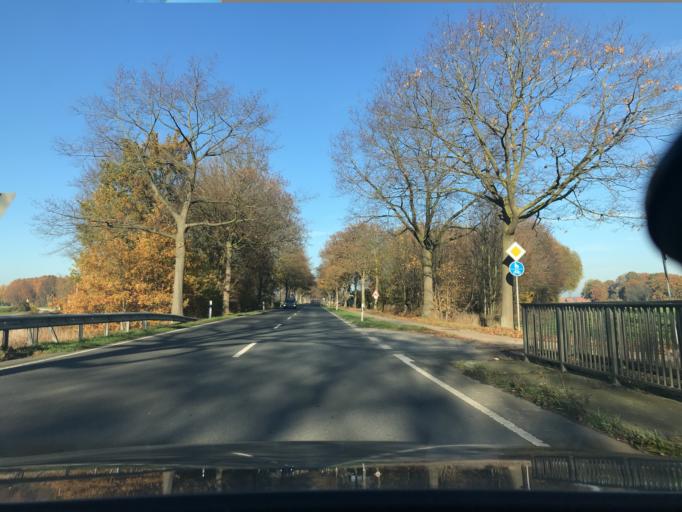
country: DE
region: North Rhine-Westphalia
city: Kempen
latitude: 51.4183
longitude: 6.4175
